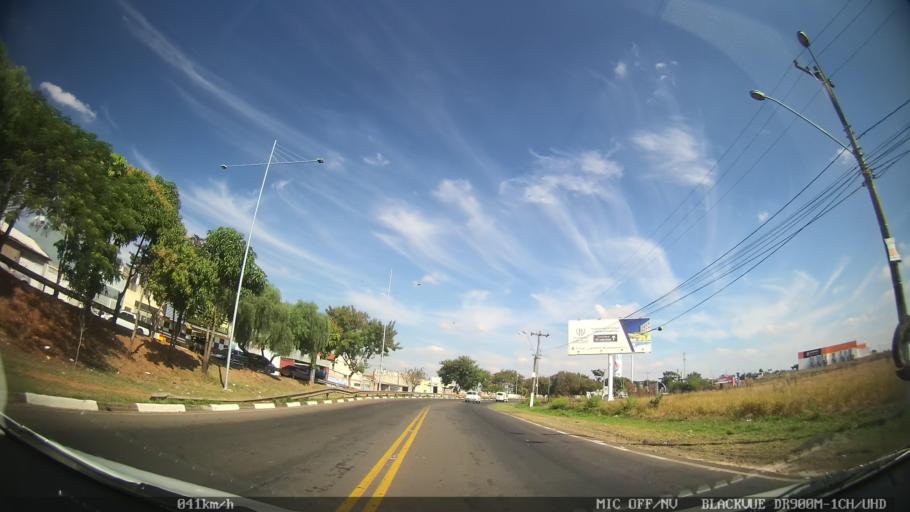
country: BR
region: Sao Paulo
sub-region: Hortolandia
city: Hortolandia
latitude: -22.8469
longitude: -47.2088
